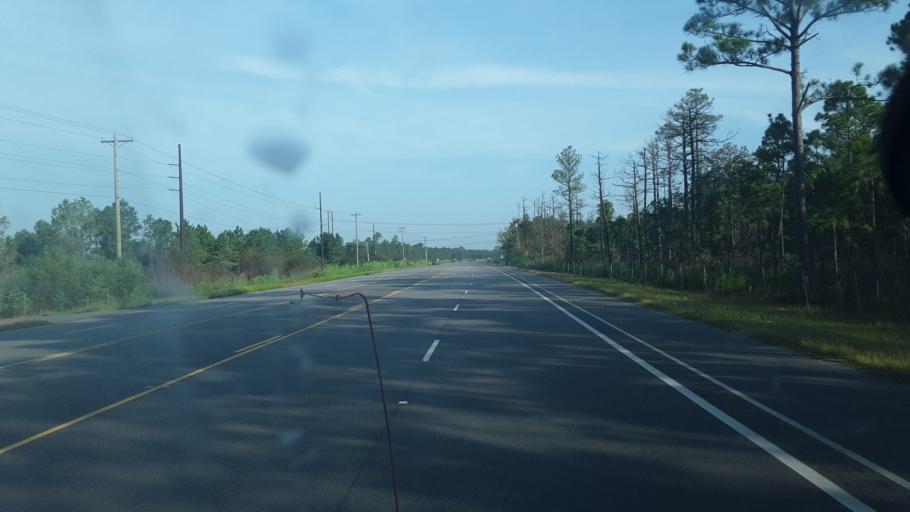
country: US
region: South Carolina
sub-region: Horry County
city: Myrtle Beach
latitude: 33.7836
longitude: -78.8763
